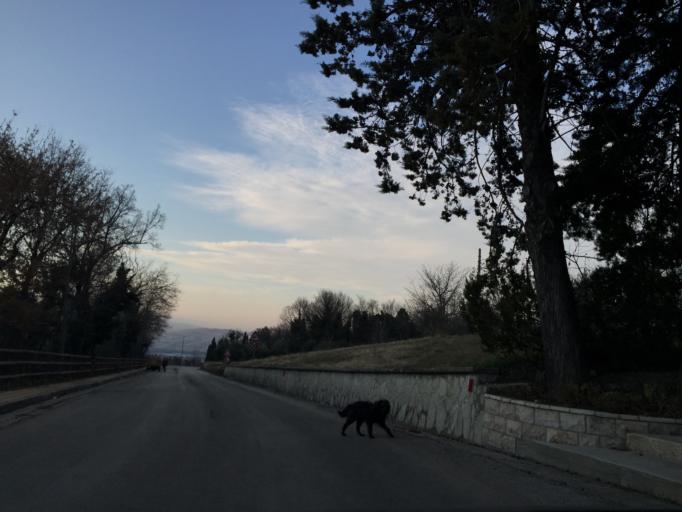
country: IT
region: Molise
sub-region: Provincia di Campobasso
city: Guardiaregia
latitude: 41.4387
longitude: 14.5464
